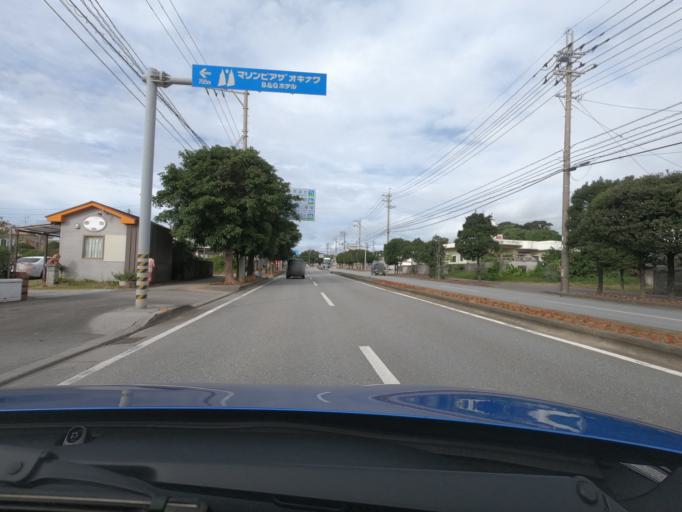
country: JP
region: Okinawa
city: Nago
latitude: 26.6763
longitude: 127.8912
